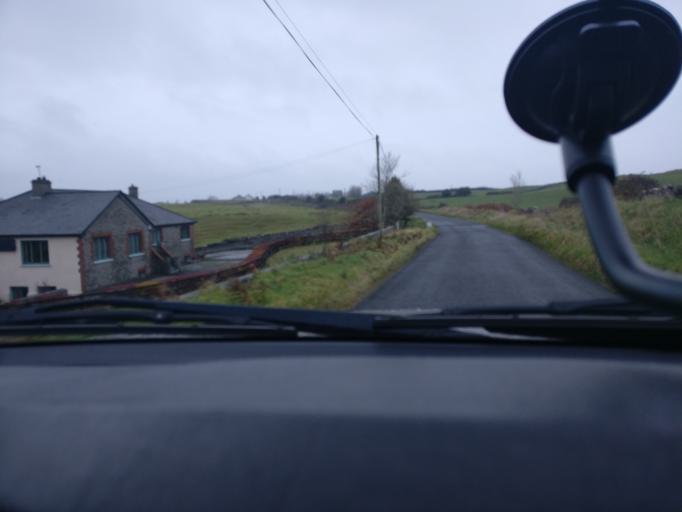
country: IE
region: Connaught
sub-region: County Galway
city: Loughrea
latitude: 53.2096
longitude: -8.5502
